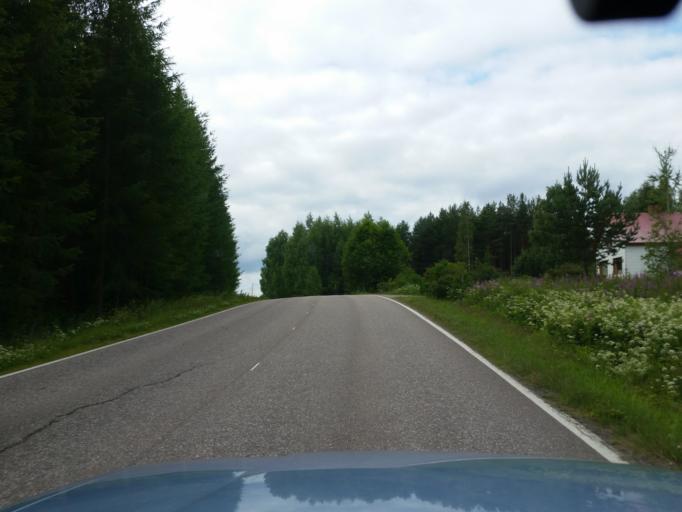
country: FI
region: Southern Savonia
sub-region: Savonlinna
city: Sulkava
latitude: 61.7943
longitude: 28.4063
